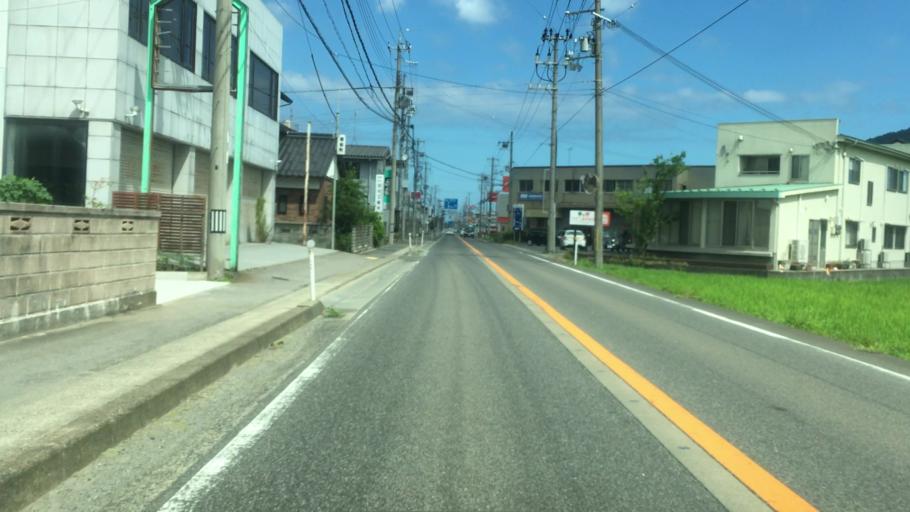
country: JP
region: Tottori
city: Tottori
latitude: 35.6125
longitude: 134.4683
